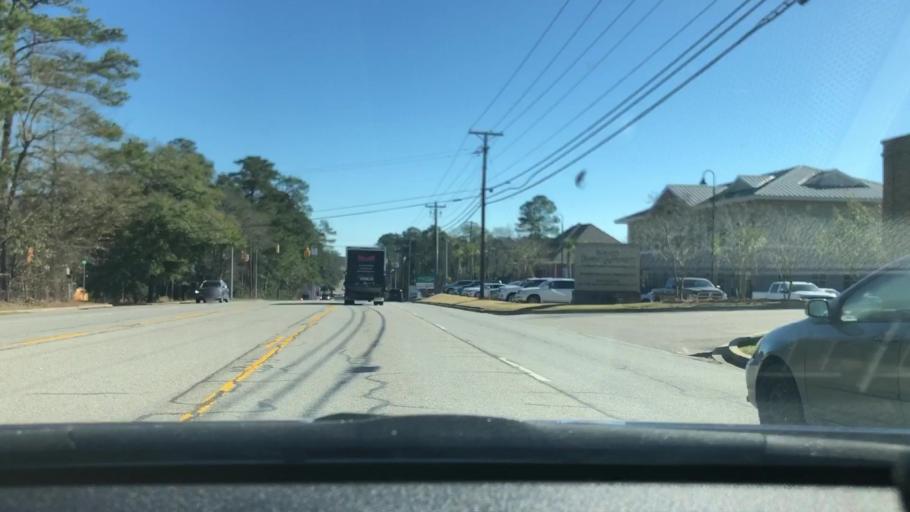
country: US
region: South Carolina
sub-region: Lexington County
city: Oak Grove
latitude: 34.0072
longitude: -81.1246
